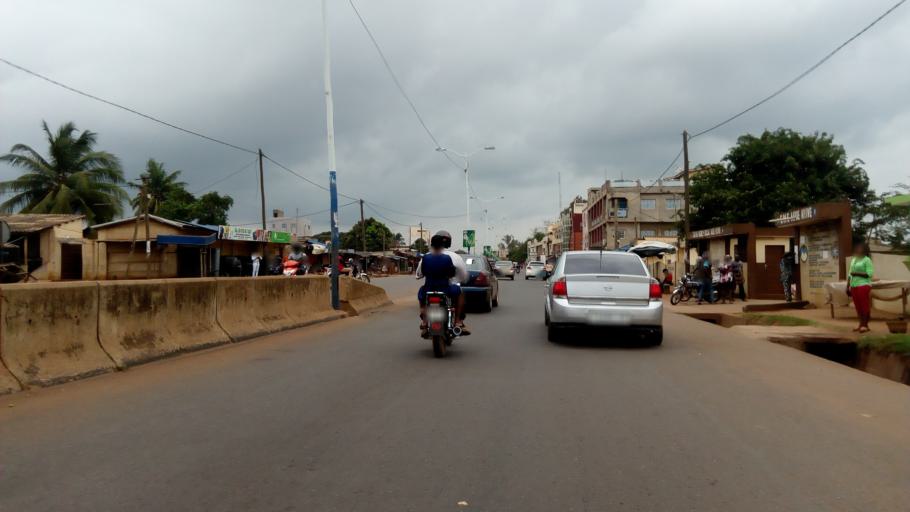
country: TG
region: Maritime
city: Lome
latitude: 6.2240
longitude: 1.2100
